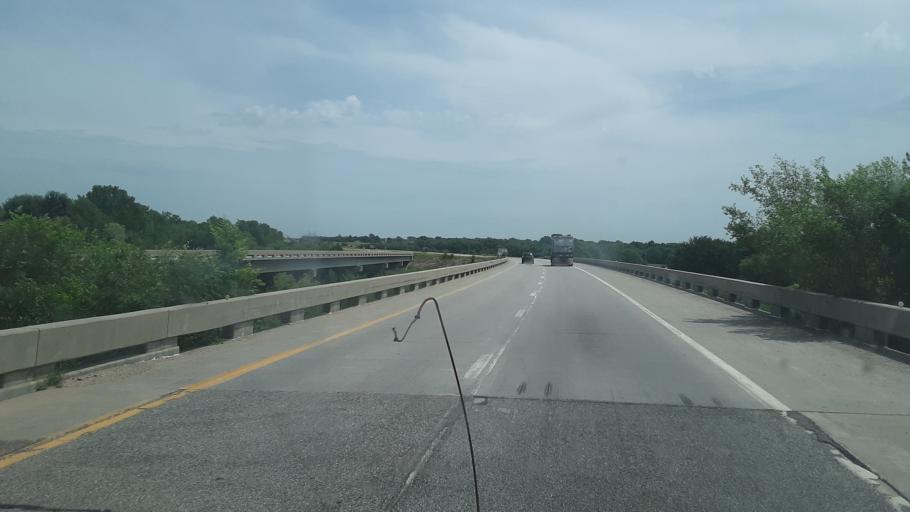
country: US
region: Kansas
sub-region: Butler County
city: Towanda
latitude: 37.7962
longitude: -97.0141
